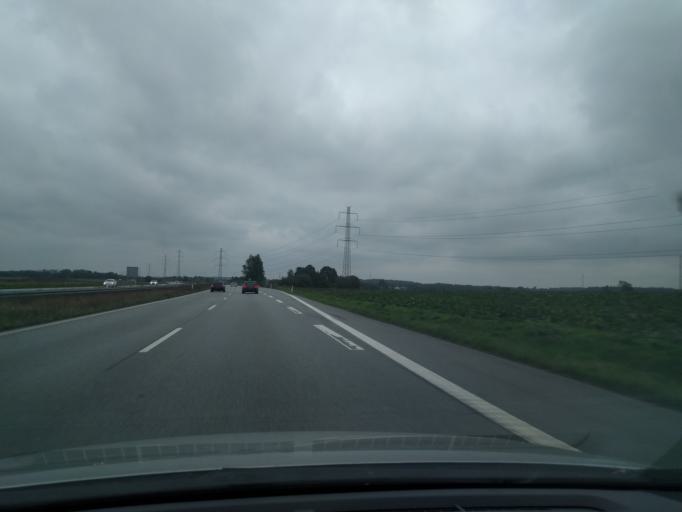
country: DK
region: Zealand
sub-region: Ringsted Kommune
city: Ringsted
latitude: 55.4561
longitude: 11.8508
